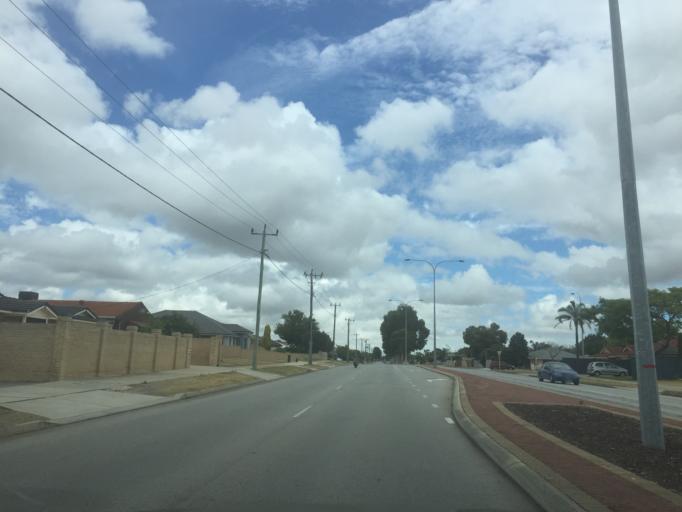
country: AU
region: Western Australia
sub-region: Gosnells
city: Thornlie
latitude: -32.0793
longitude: 115.9562
